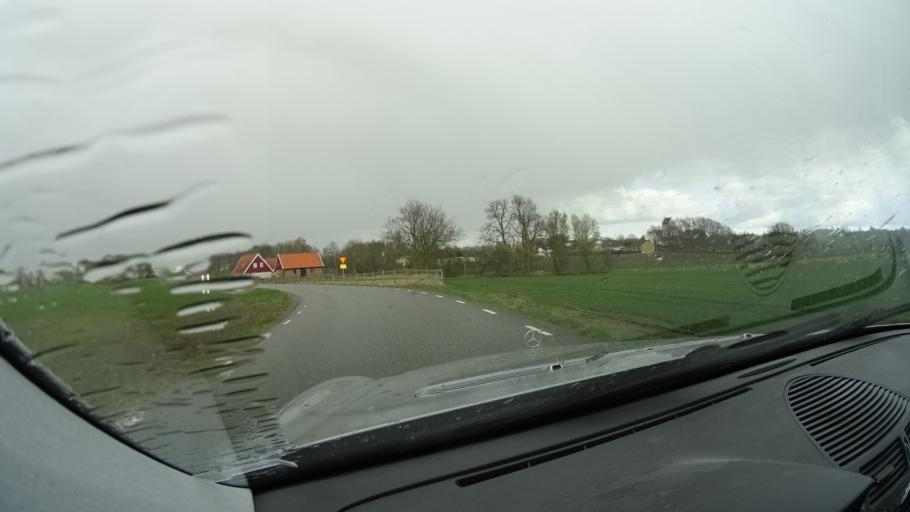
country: SE
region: Skane
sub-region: Lunds Kommun
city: Lund
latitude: 55.7429
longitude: 13.1682
